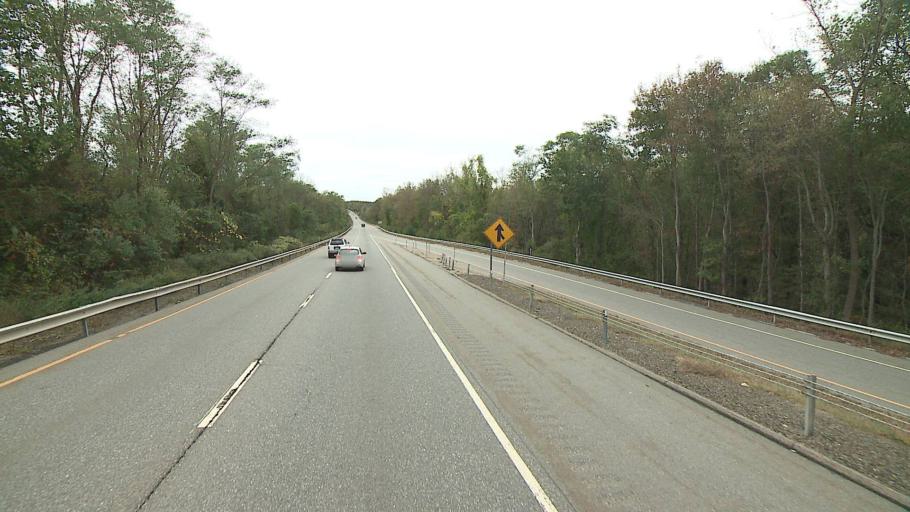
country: US
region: Connecticut
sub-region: Middlesex County
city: Deep River Center
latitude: 41.3823
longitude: -72.4462
